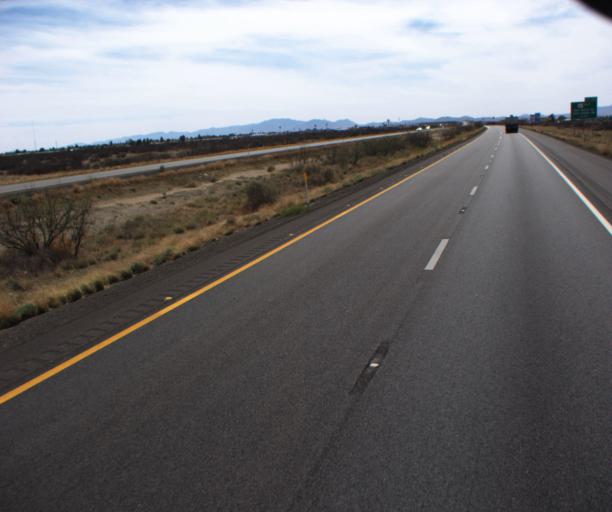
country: US
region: Arizona
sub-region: Cochise County
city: Willcox
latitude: 32.2780
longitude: -109.8337
